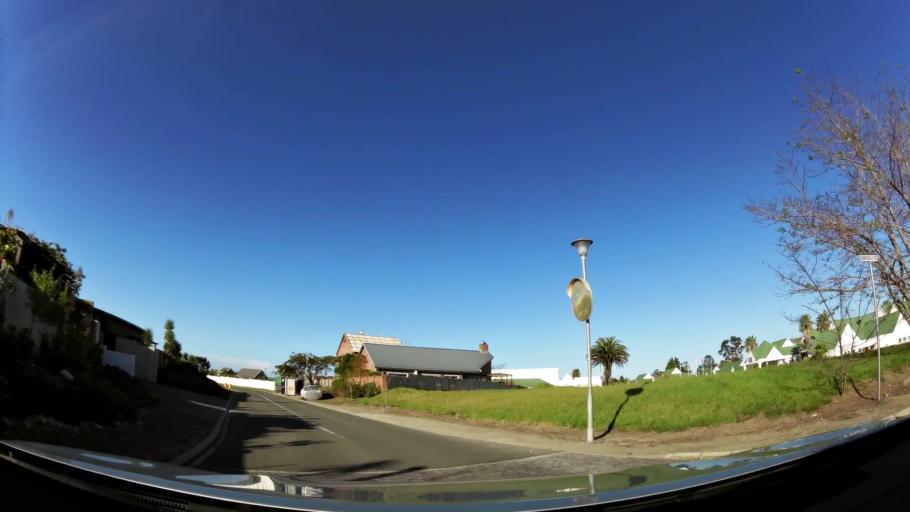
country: ZA
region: Western Cape
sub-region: Eden District Municipality
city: George
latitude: -33.9589
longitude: 22.4440
